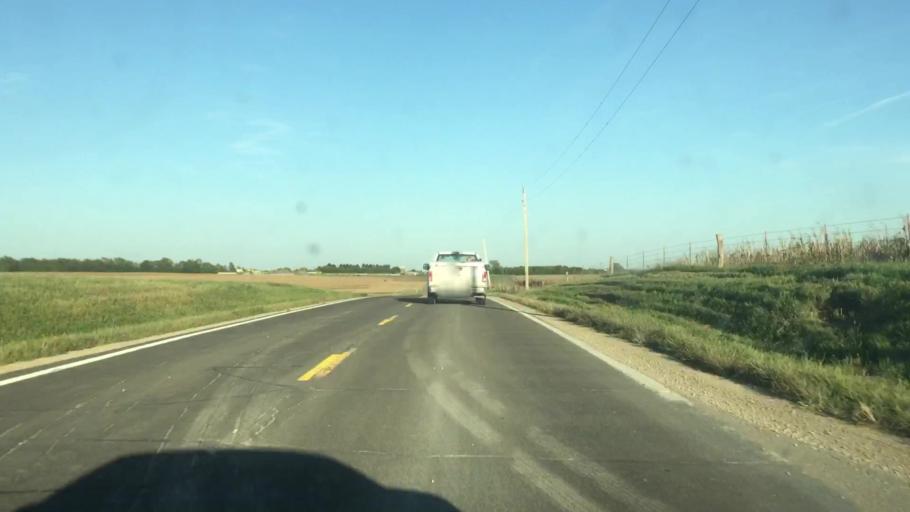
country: US
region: Kansas
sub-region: Brown County
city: Horton
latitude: 39.5513
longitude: -95.4207
